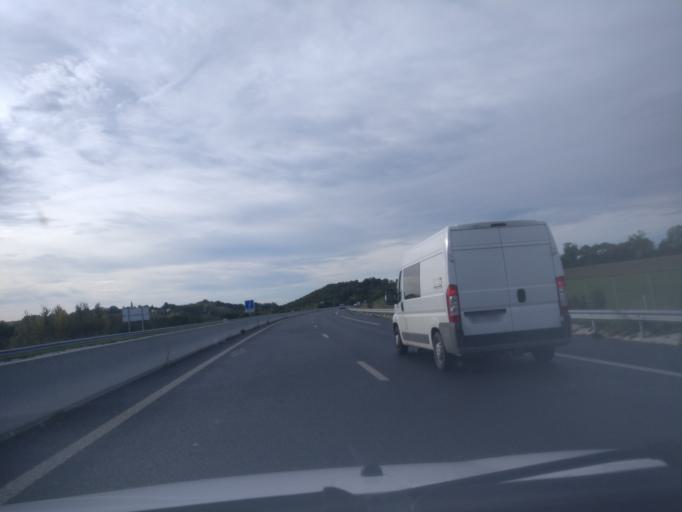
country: FR
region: Lower Normandy
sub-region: Departement de la Manche
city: Sartilly
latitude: 48.7498
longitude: -1.4420
